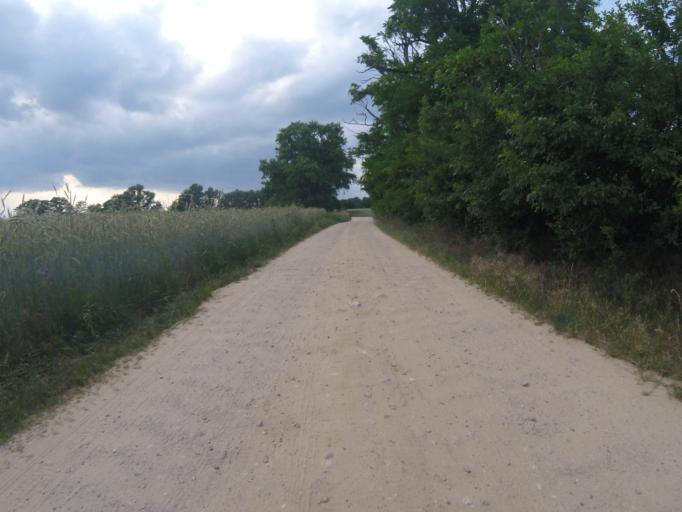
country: DE
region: Brandenburg
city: Bestensee
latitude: 52.2540
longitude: 13.6235
